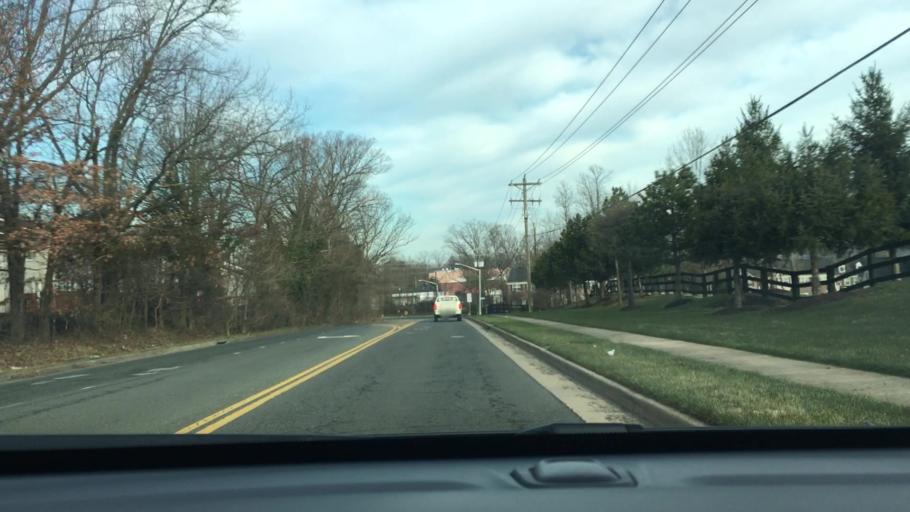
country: US
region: Virginia
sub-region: Prince William County
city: Yorkshire
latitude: 38.7730
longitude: -77.4482
